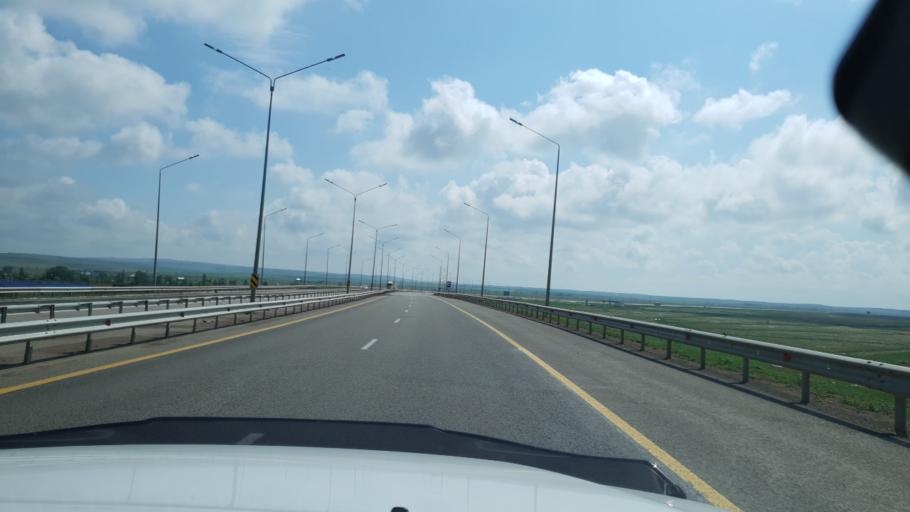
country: KZ
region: Qaraghandy
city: Osakarovka
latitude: 50.8113
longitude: 72.1791
